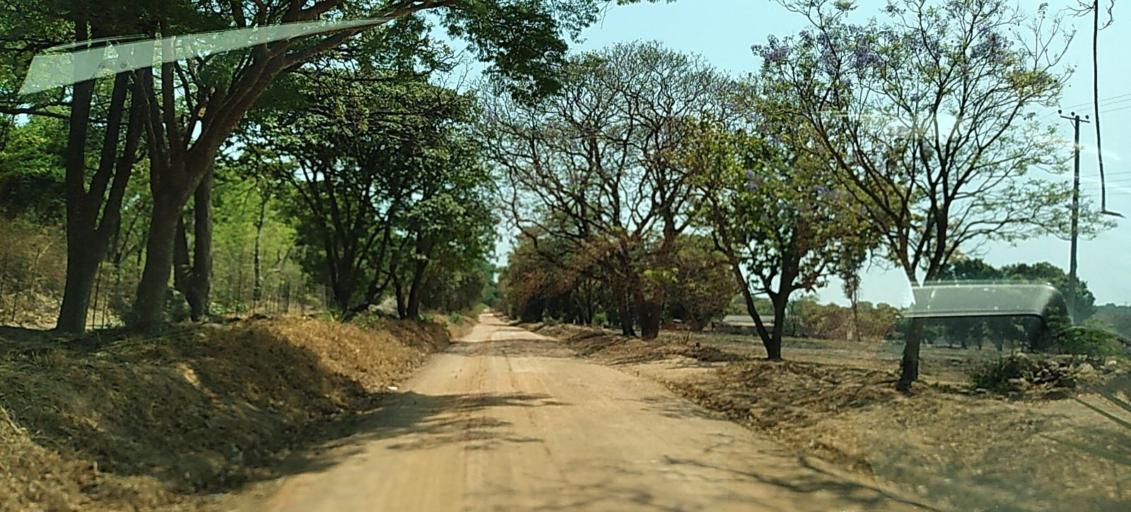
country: ZM
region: Copperbelt
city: Chambishi
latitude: -12.6062
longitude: 27.9536
